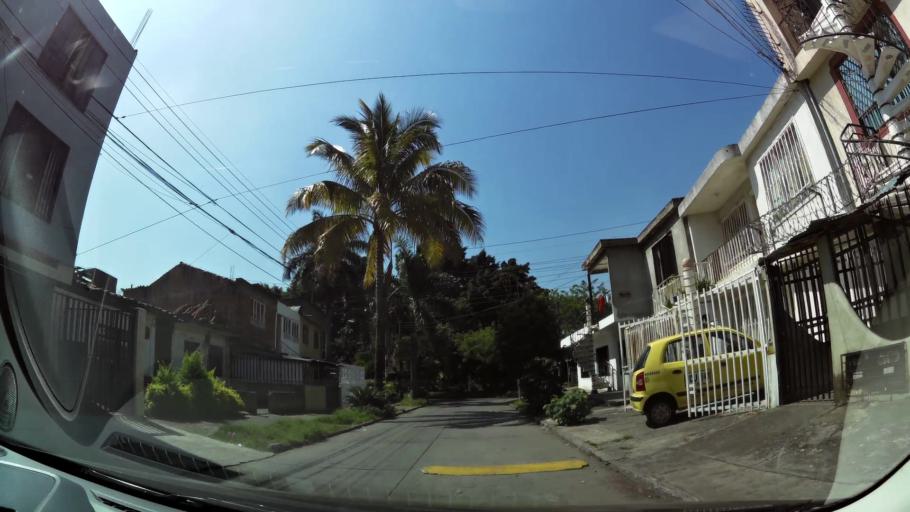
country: CO
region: Valle del Cauca
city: Cali
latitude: 3.4065
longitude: -76.5254
